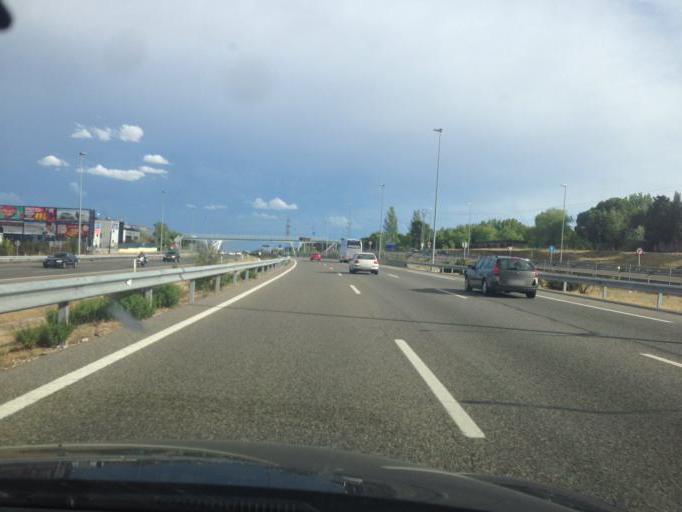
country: ES
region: Madrid
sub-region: Provincia de Madrid
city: Las Rozas de Madrid
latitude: 40.5189
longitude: -3.8856
